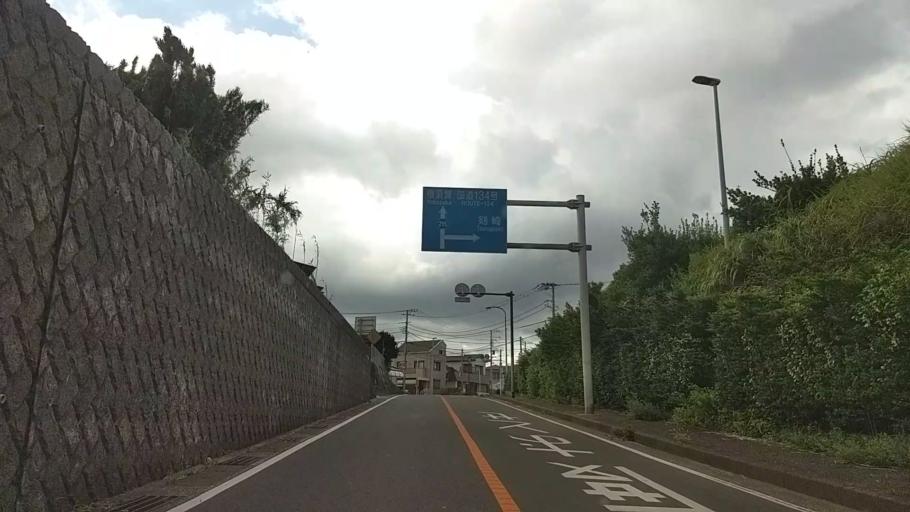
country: JP
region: Kanagawa
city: Miura
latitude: 35.1460
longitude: 139.6705
